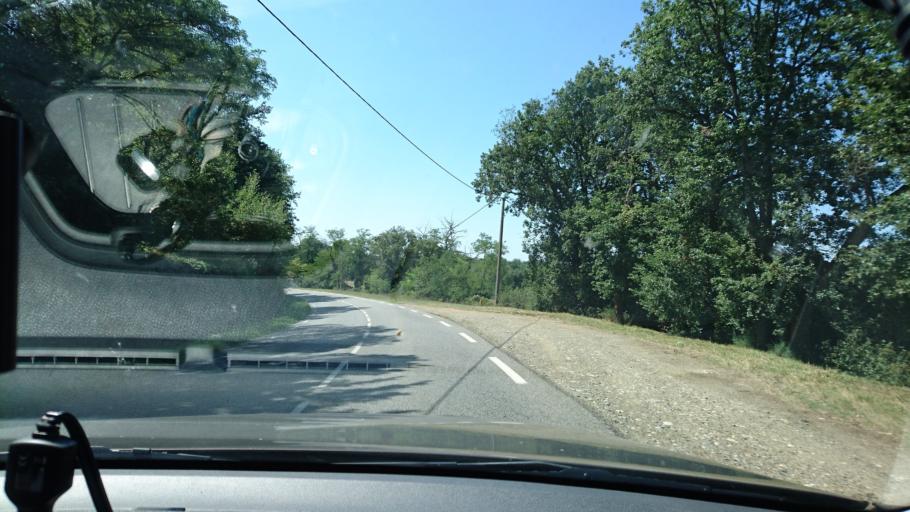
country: FR
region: Midi-Pyrenees
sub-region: Departement de la Haute-Garonne
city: Noe
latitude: 43.3403
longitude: 1.2709
